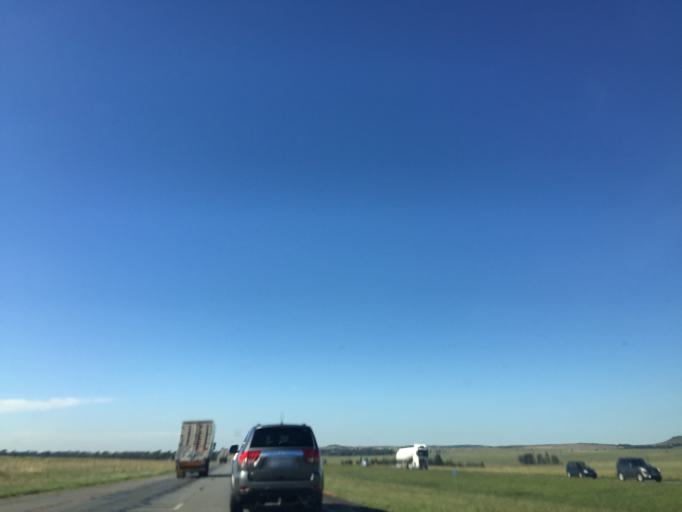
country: ZA
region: Gauteng
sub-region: Ekurhuleni Metropolitan Municipality
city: Germiston
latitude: -26.3858
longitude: 28.0866
